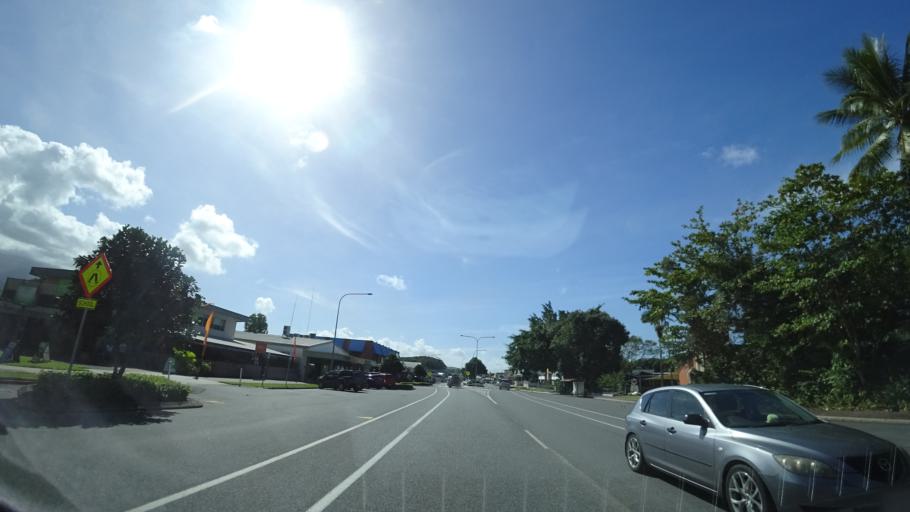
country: AU
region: Queensland
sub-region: Cairns
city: Port Douglas
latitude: -16.4627
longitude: 145.3734
